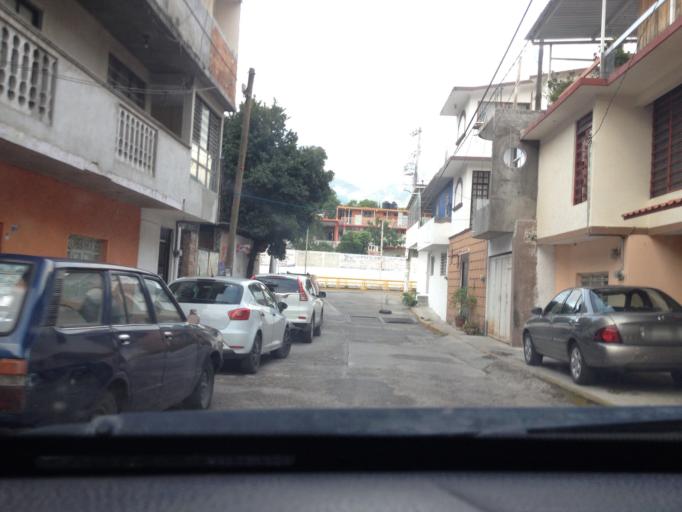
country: MX
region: Guerrero
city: Chilpancingo de los Bravos
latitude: 17.5504
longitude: -99.5041
